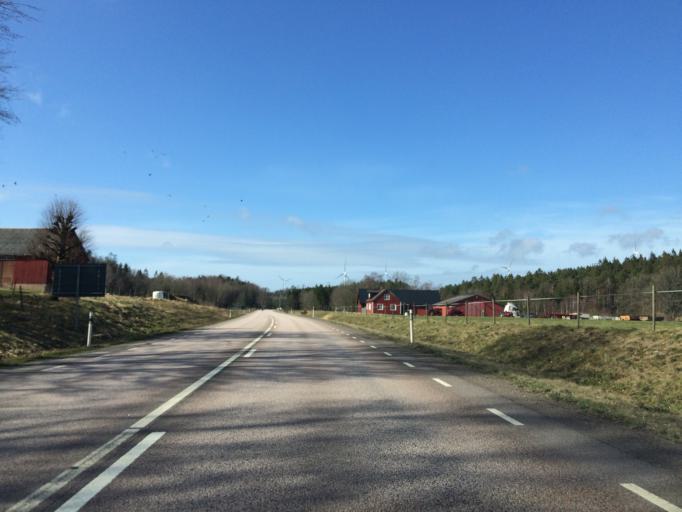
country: SE
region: Halland
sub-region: Laholms Kommun
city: Knared
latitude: 56.5270
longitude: 13.2430
